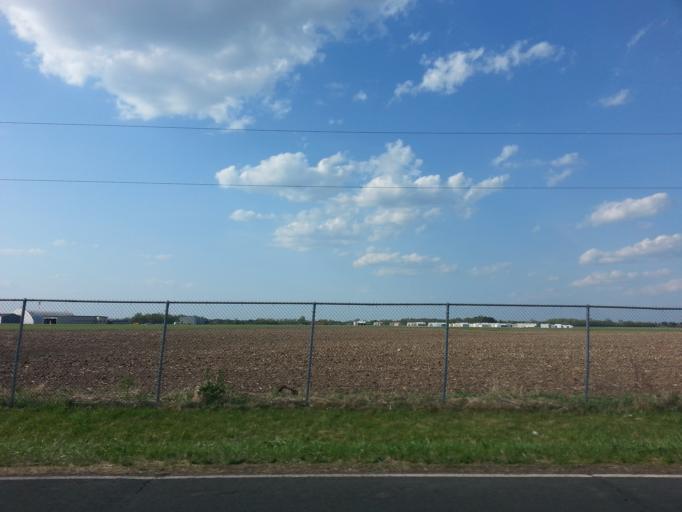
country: US
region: Minnesota
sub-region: Washington County
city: Lake Elmo
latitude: 44.9925
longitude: -92.8577
